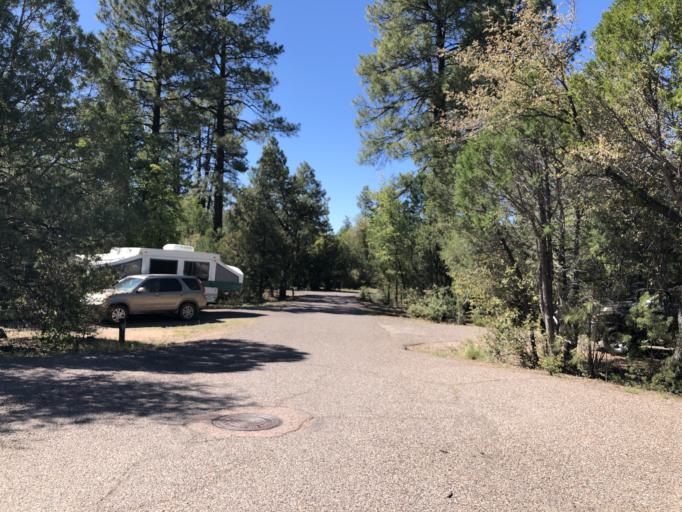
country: US
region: Arizona
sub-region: Gila County
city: Payson
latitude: 34.2701
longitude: -111.3200
